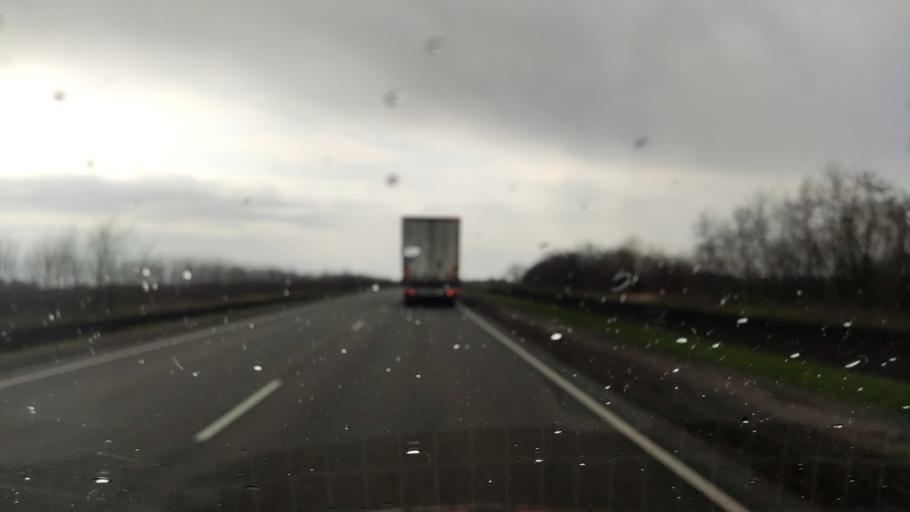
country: RU
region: Voronezj
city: Nizhnedevitsk
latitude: 51.5667
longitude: 38.3437
